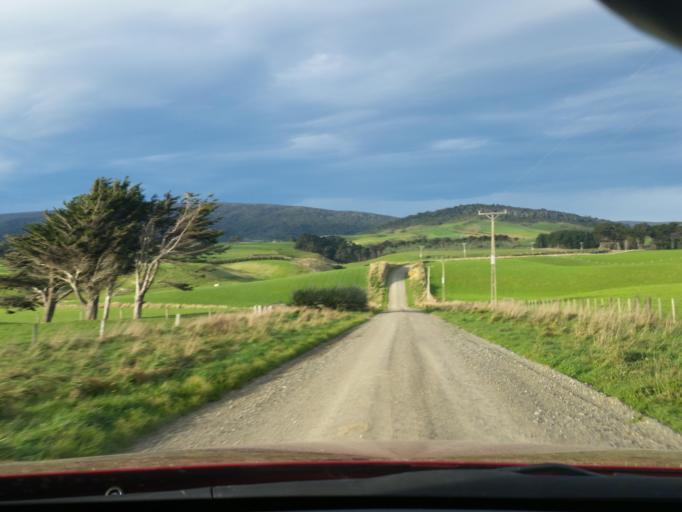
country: NZ
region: Southland
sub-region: Southland District
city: Riverton
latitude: -46.2964
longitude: 167.7517
